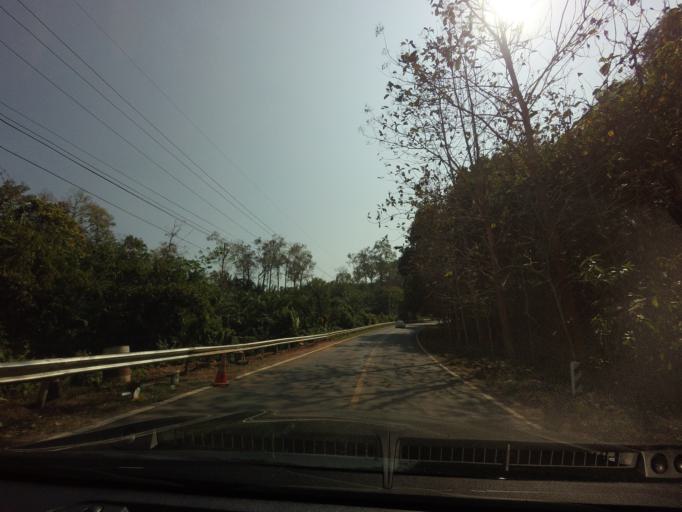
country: TH
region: Kanchanaburi
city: Thong Pha Phum
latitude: 14.6542
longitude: 98.5551
